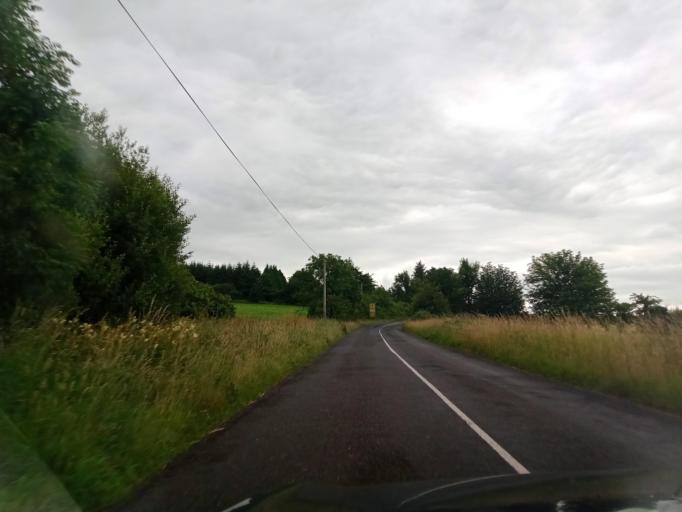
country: IE
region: Leinster
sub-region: Laois
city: Stradbally
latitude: 52.9254
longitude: -7.1940
